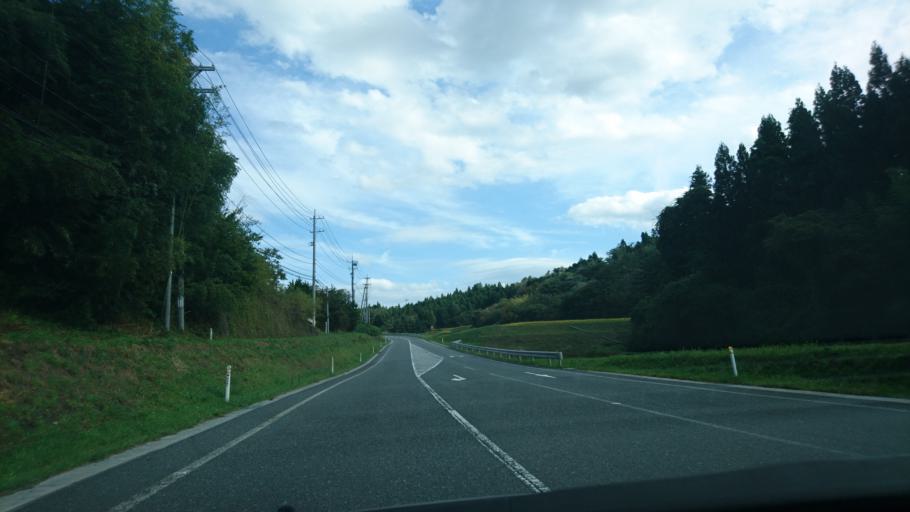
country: JP
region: Iwate
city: Ichinoseki
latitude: 38.8330
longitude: 141.2179
